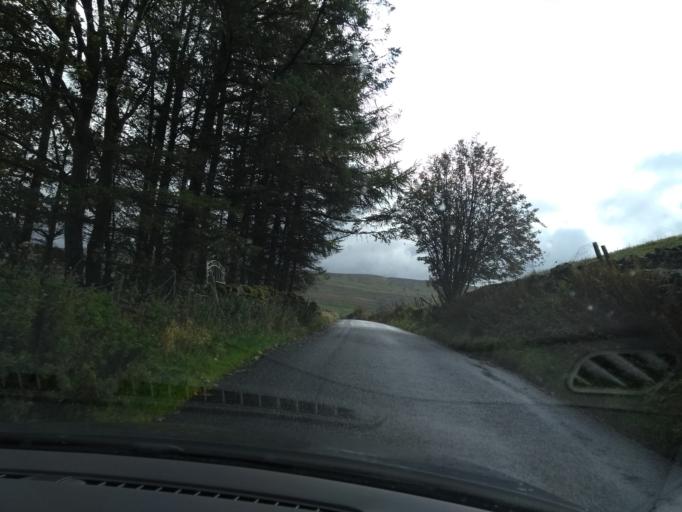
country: GB
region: England
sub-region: Cumbria
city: Kirkby Stephen
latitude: 54.3854
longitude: -2.1733
